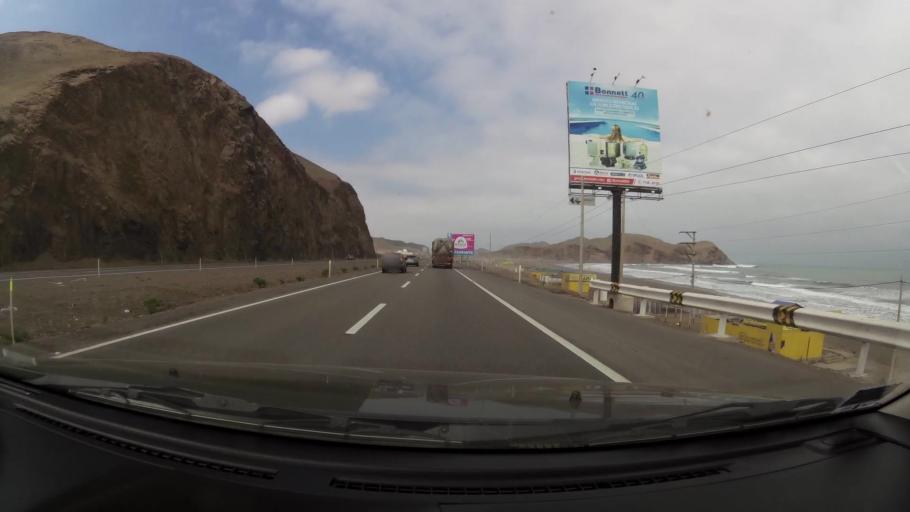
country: PE
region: Lima
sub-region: Provincia de Canete
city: Mala
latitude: -12.6384
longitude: -76.6695
